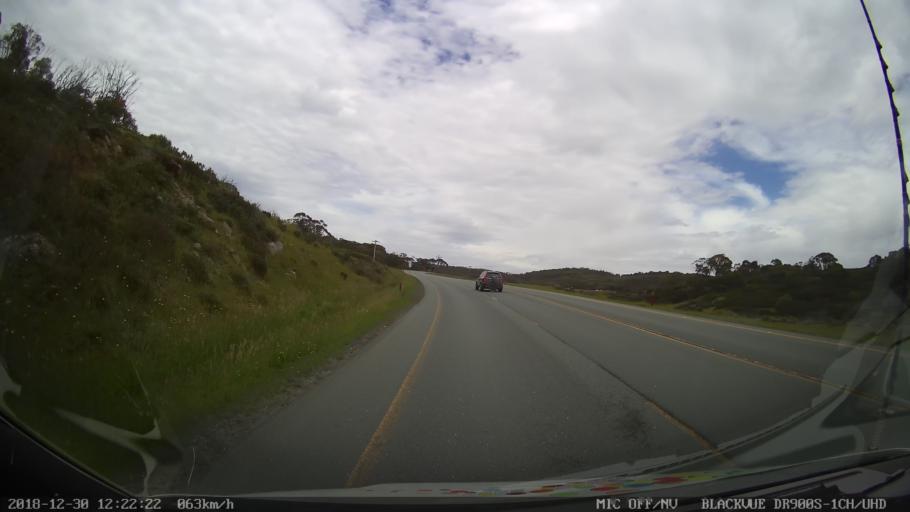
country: AU
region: New South Wales
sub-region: Snowy River
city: Jindabyne
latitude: -36.3585
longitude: 148.5106
